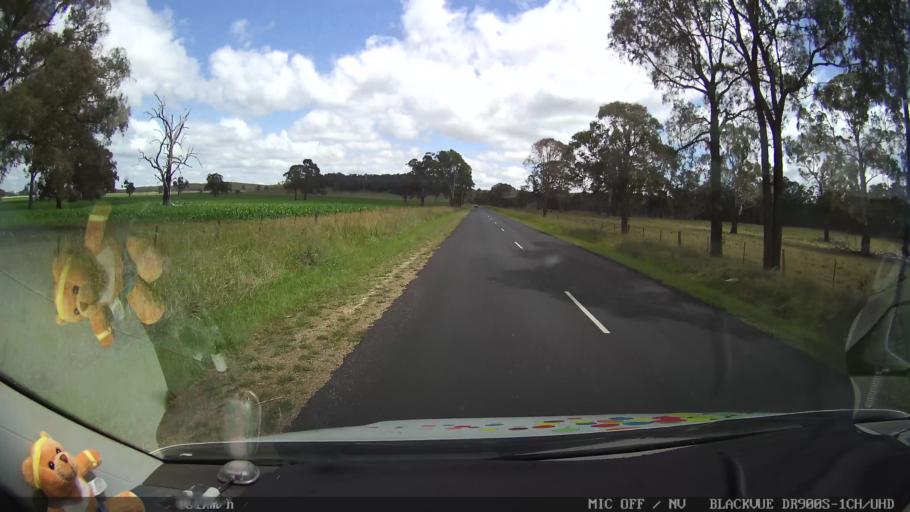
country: AU
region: New South Wales
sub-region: Glen Innes Severn
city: Glen Innes
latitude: -29.6016
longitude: 151.6665
